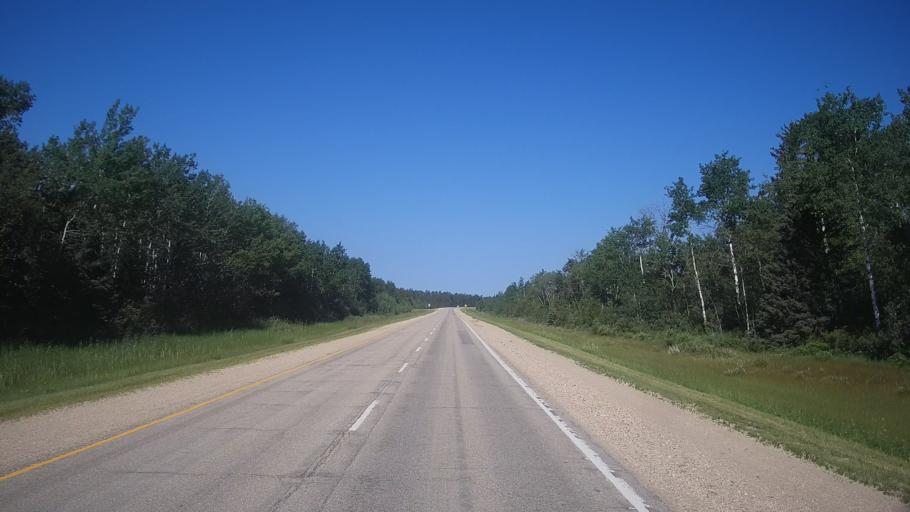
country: CA
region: Manitoba
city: La Broquerie
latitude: 49.6494
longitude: -95.9628
